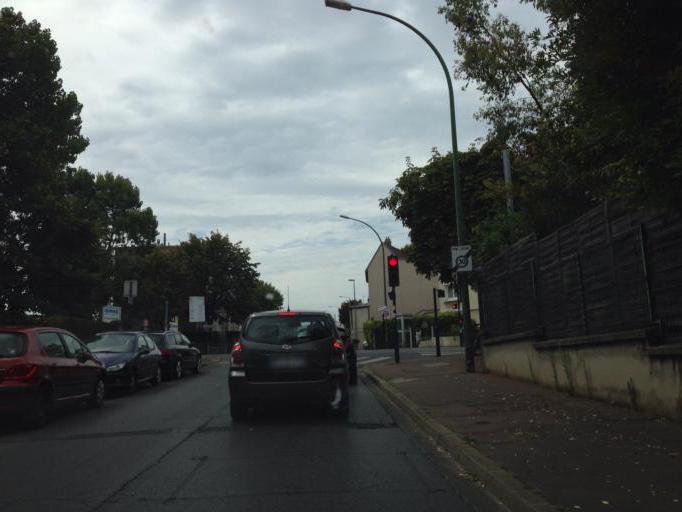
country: FR
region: Ile-de-France
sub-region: Departement des Hauts-de-Seine
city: Issy-les-Moulineaux
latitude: 48.8143
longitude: 2.2708
